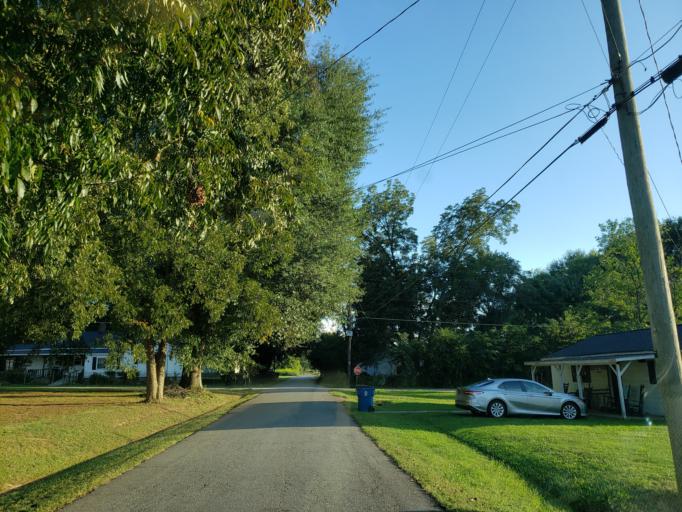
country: US
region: Georgia
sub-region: Bartow County
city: Euharlee
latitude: 34.2350
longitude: -84.9476
